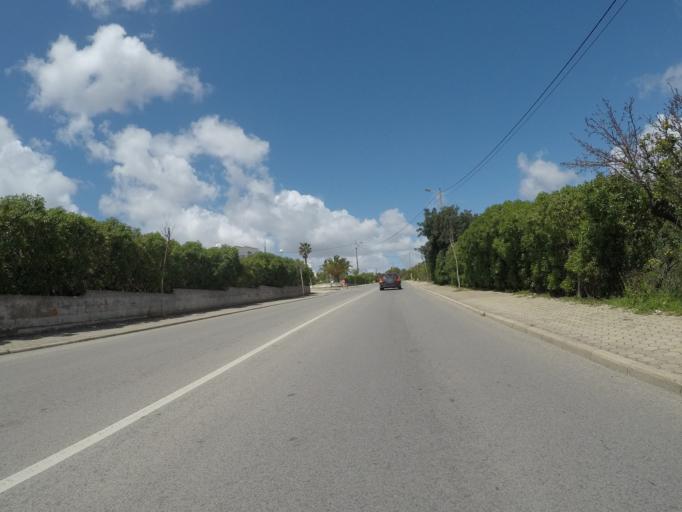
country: PT
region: Faro
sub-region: Silves
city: Armacao de Pera
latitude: 37.1042
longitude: -8.3747
